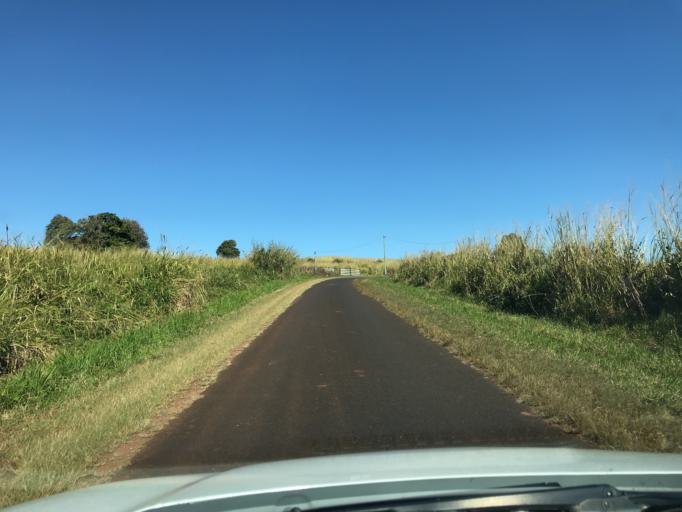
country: AU
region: Queensland
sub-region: Tablelands
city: Atherton
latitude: -17.2907
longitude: 145.5444
